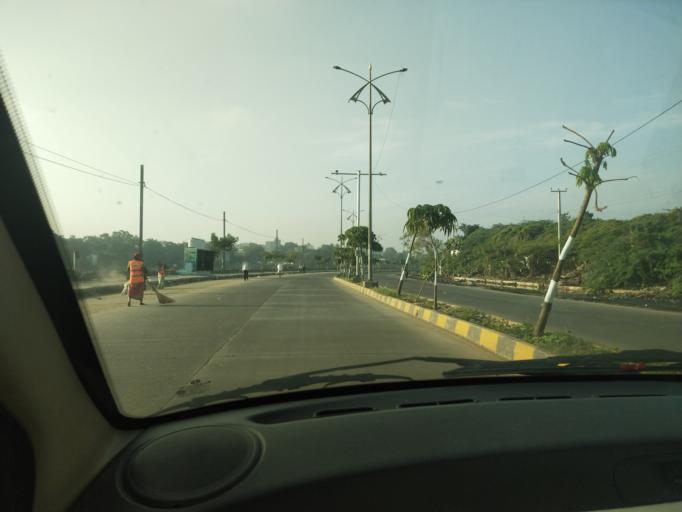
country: IN
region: Telangana
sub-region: Hyderabad
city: Hyderabad
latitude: 17.3641
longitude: 78.4552
